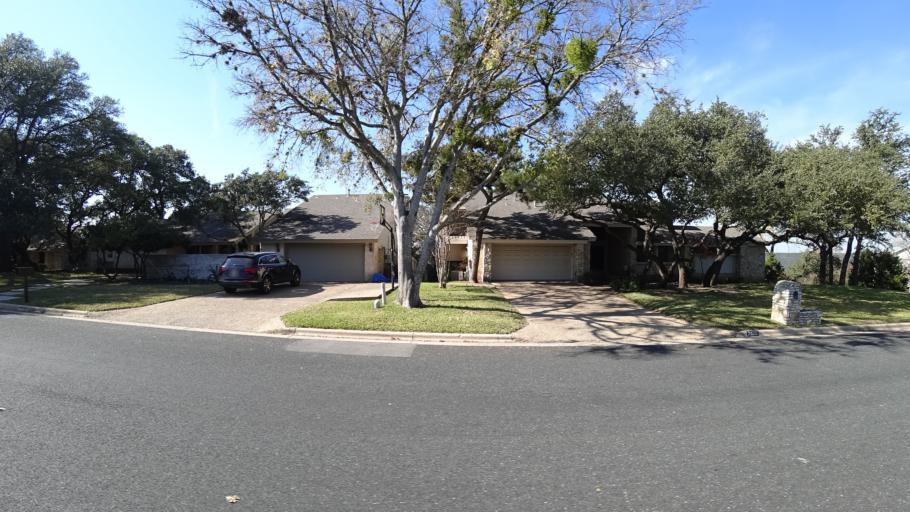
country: US
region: Texas
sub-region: Williamson County
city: Jollyville
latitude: 30.3697
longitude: -97.7755
